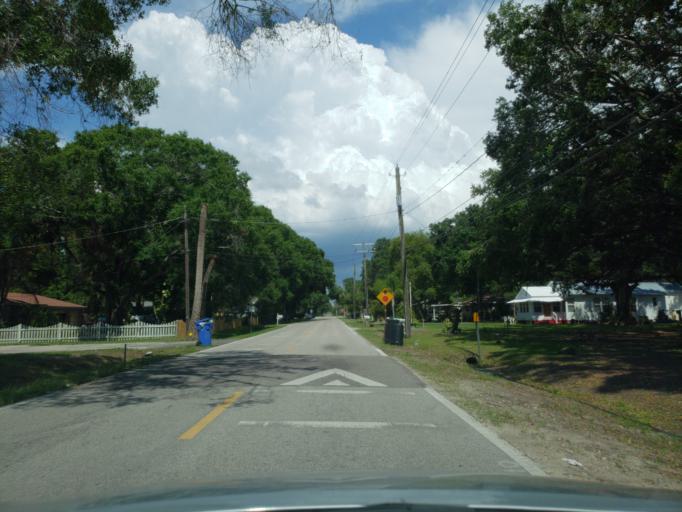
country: US
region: Florida
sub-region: Hillsborough County
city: Palm River-Clair Mel
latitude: 27.9335
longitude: -82.3869
